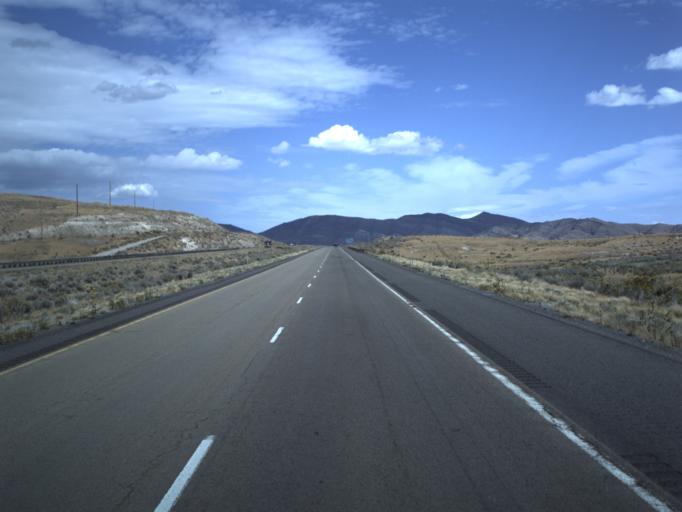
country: US
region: Utah
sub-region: Tooele County
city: Grantsville
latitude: 40.8158
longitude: -112.9171
